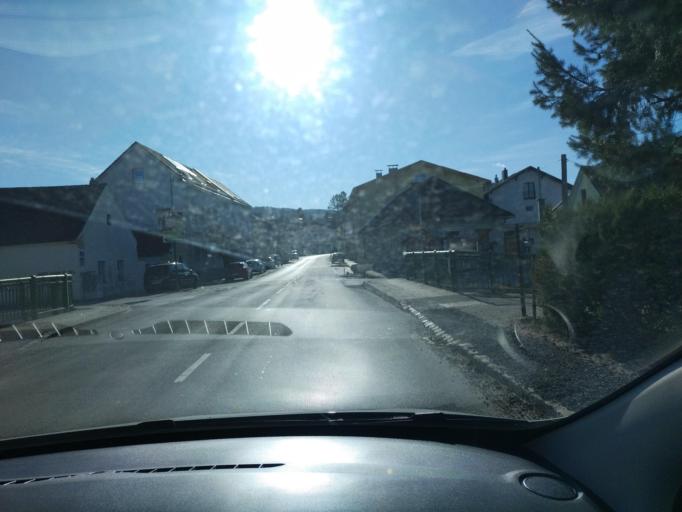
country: AT
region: Lower Austria
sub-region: Politischer Bezirk Wiener Neustadt
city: Lanzenkirchen
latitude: 47.7474
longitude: 16.2532
